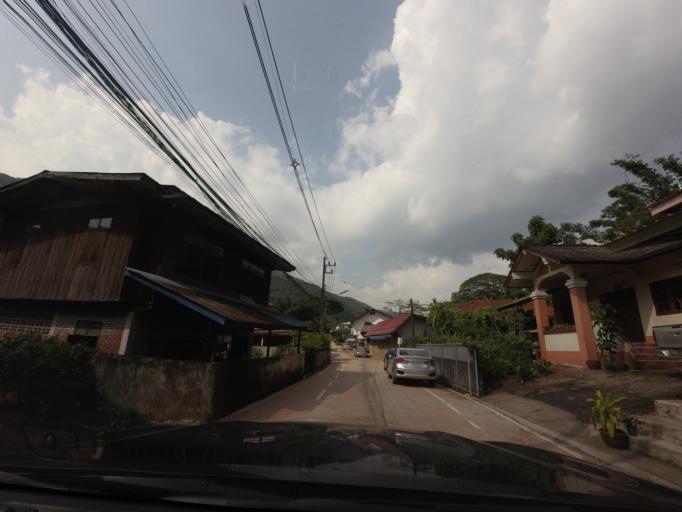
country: TH
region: Nan
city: Bo Kluea
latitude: 19.1508
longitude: 101.1554
